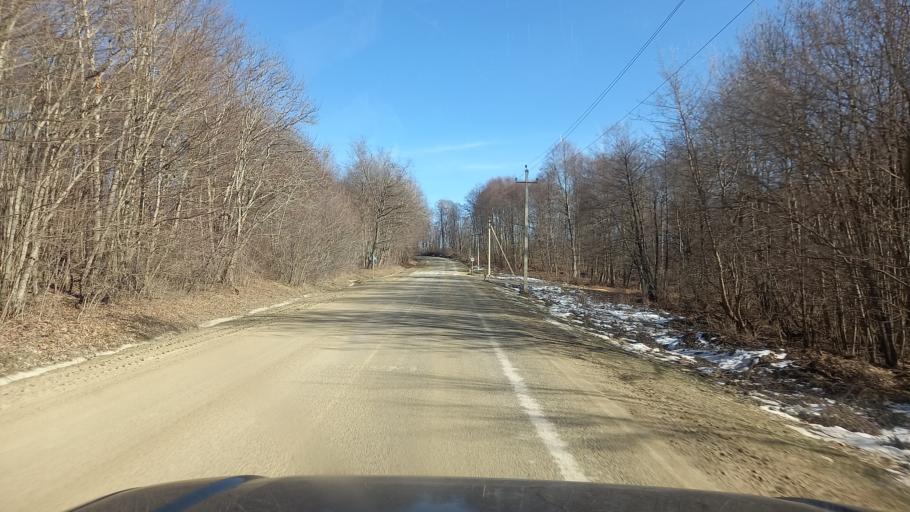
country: RU
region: Adygeya
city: Kamennomostskiy
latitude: 44.2793
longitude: 40.2893
